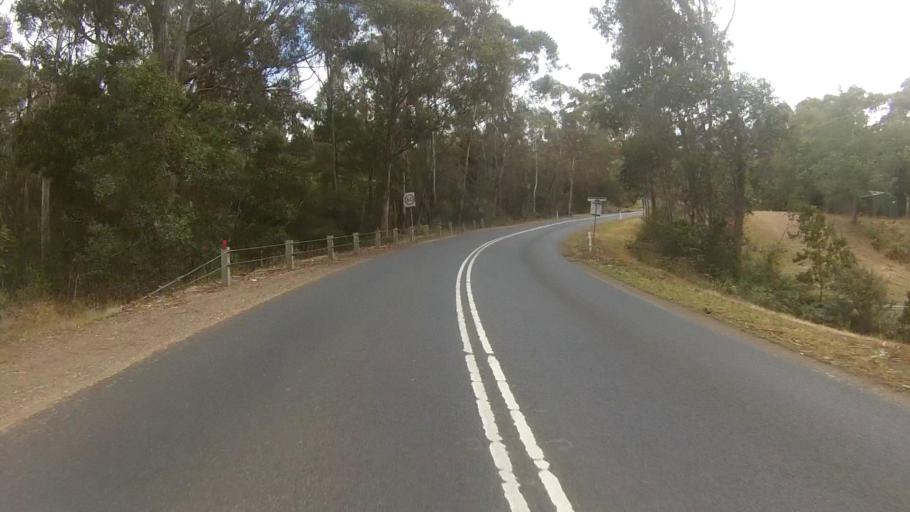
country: AU
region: Tasmania
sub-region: Kingborough
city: Margate
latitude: -43.0134
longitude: 147.2431
